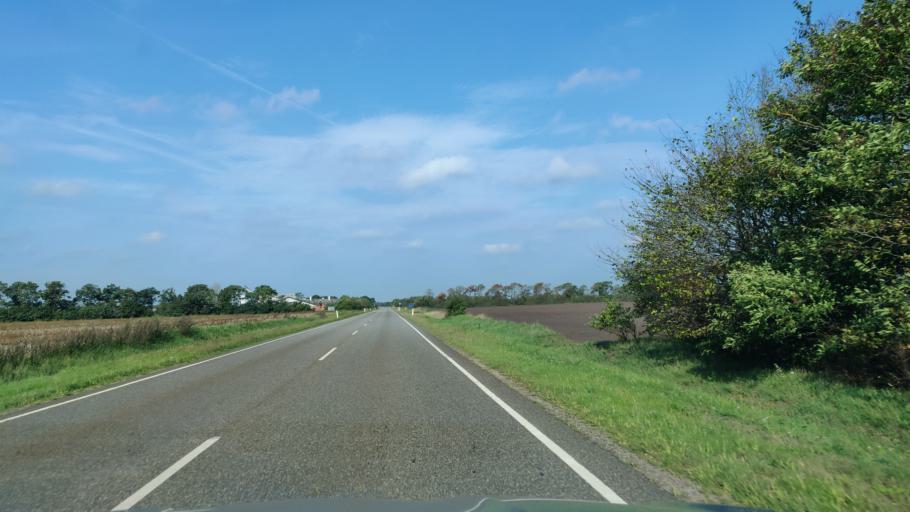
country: DK
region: Central Jutland
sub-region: Herning Kommune
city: Sunds
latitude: 56.2578
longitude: 9.0390
